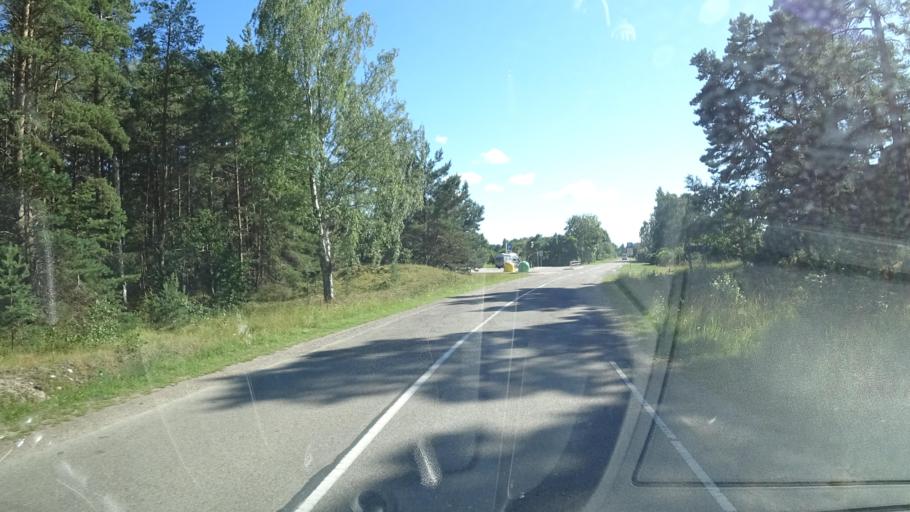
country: LV
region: Rojas
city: Roja
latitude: 57.7517
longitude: 22.5960
